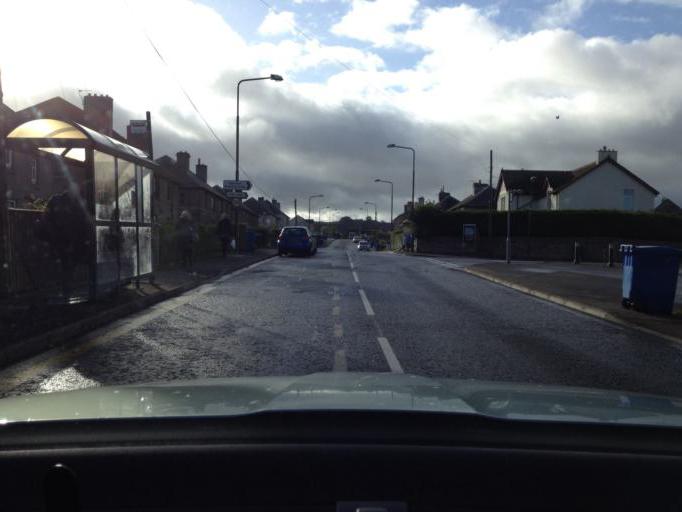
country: GB
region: Scotland
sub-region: West Lothian
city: East Calder
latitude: 55.8921
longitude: -3.4639
